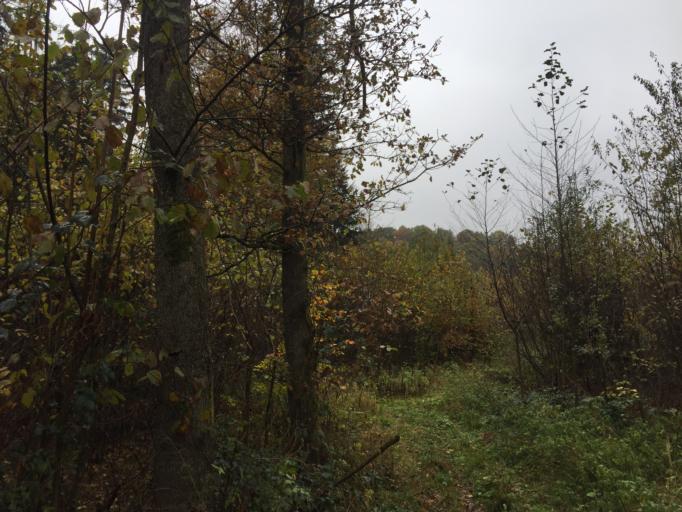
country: AT
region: Styria
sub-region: Politischer Bezirk Graz-Umgebung
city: Hart bei Graz
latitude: 47.0689
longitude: 15.5403
